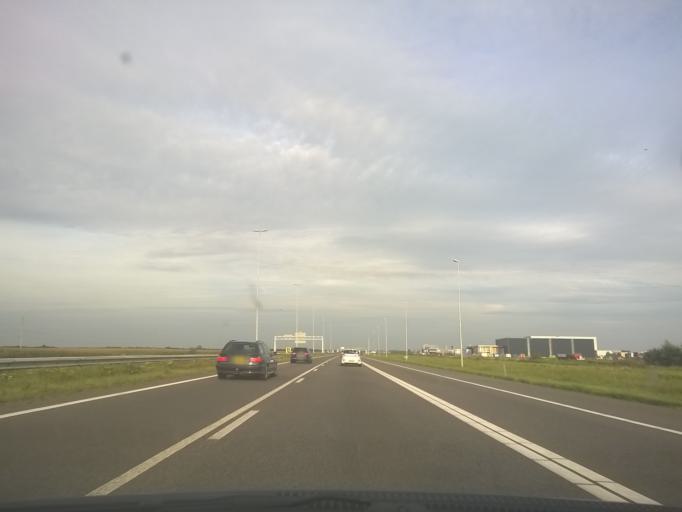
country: NL
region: Friesland
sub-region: Gemeente Heerenveen
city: Heerenveen
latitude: 52.9777
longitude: 5.9249
